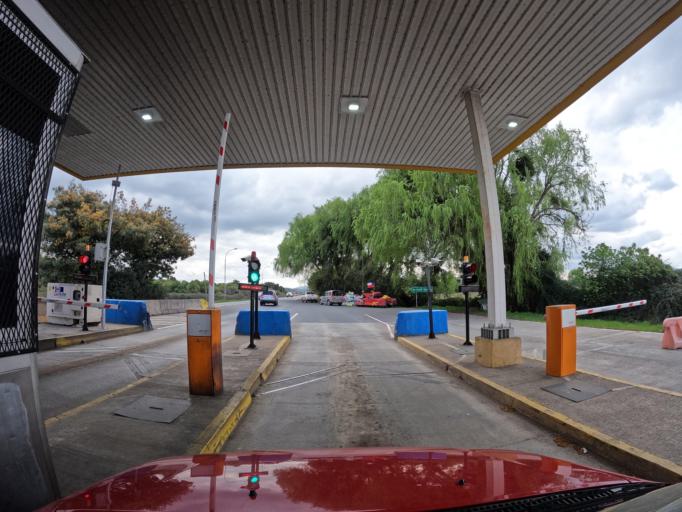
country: CL
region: Maule
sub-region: Provincia de Linares
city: San Javier
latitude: -35.6336
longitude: -71.7067
